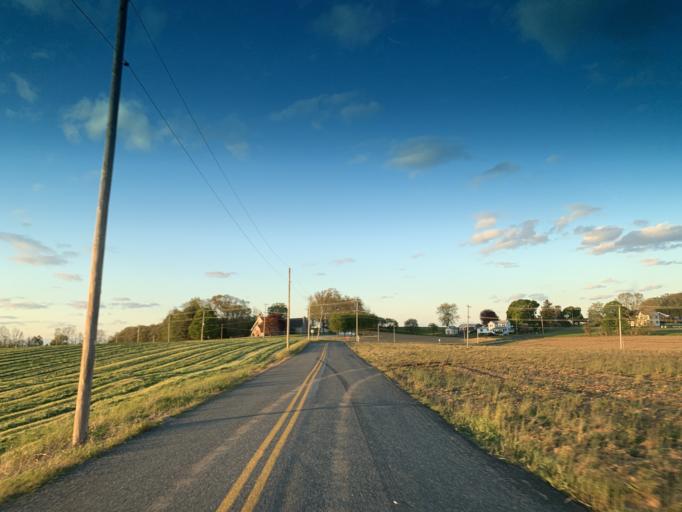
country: US
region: Maryland
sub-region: Harford County
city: Jarrettsville
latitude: 39.6633
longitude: -76.4093
